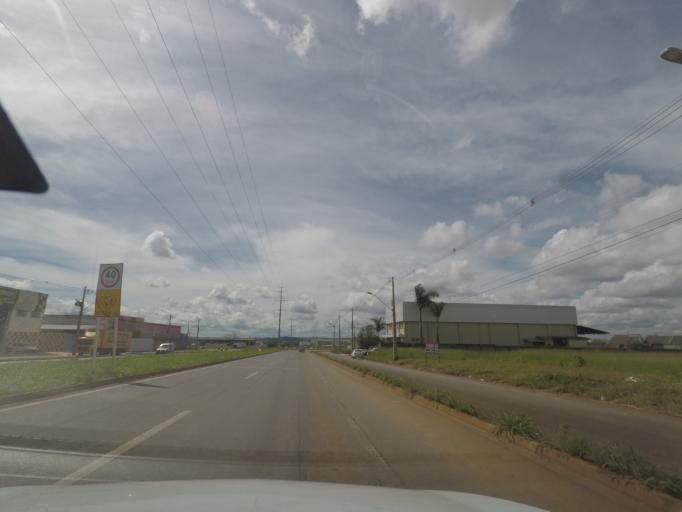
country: BR
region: Goias
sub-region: Goiania
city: Goiania
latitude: -16.7306
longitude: -49.3496
